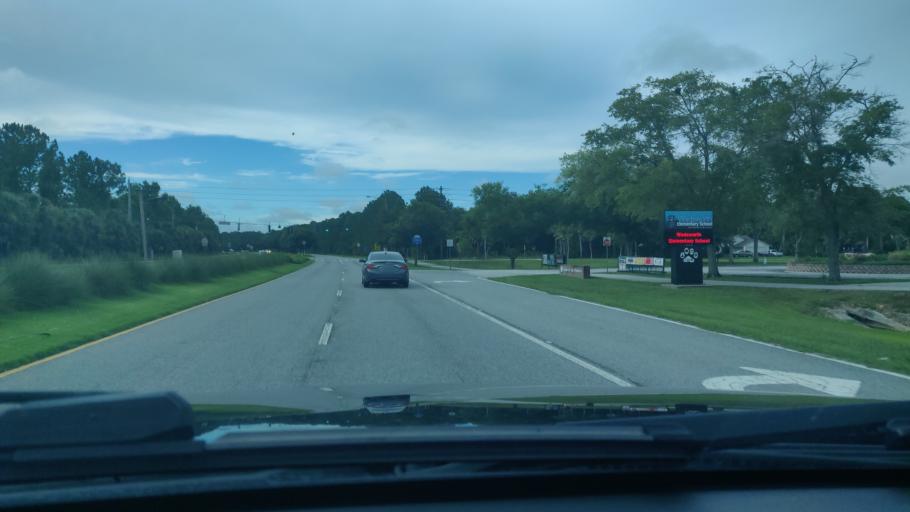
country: US
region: Florida
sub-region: Flagler County
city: Palm Coast
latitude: 29.5317
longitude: -81.2252
